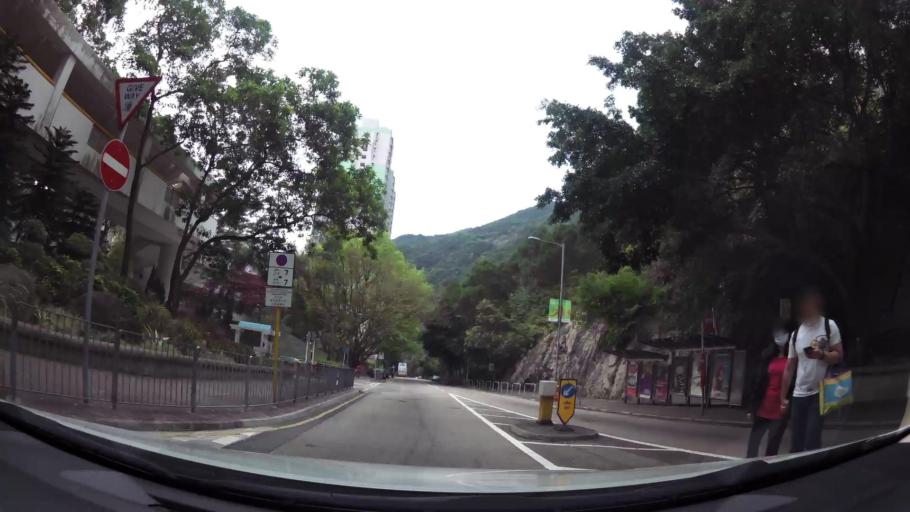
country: HK
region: Wanchai
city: Wan Chai
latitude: 22.2775
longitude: 114.2234
